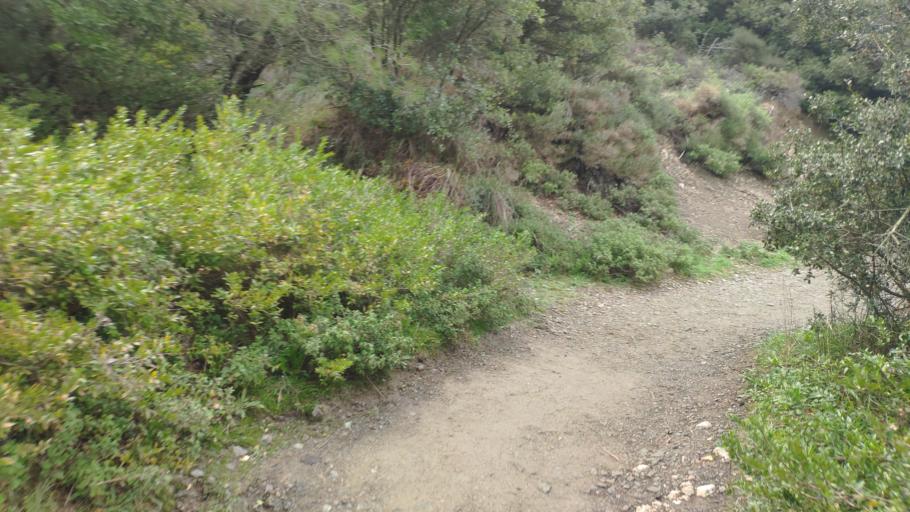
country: GR
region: Attica
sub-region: Nomarchia Anatolikis Attikis
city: Afidnes
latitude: 38.2140
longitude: 23.8052
